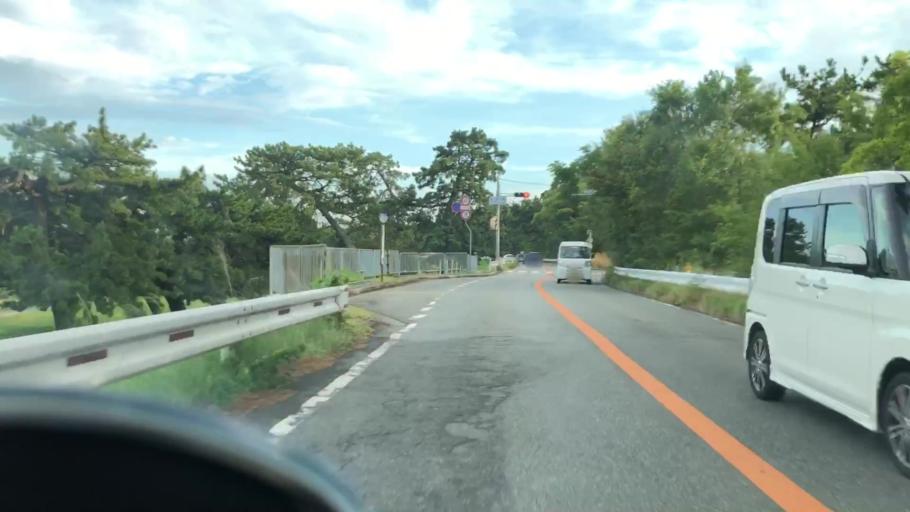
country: JP
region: Hyogo
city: Itami
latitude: 34.7596
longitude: 135.3720
